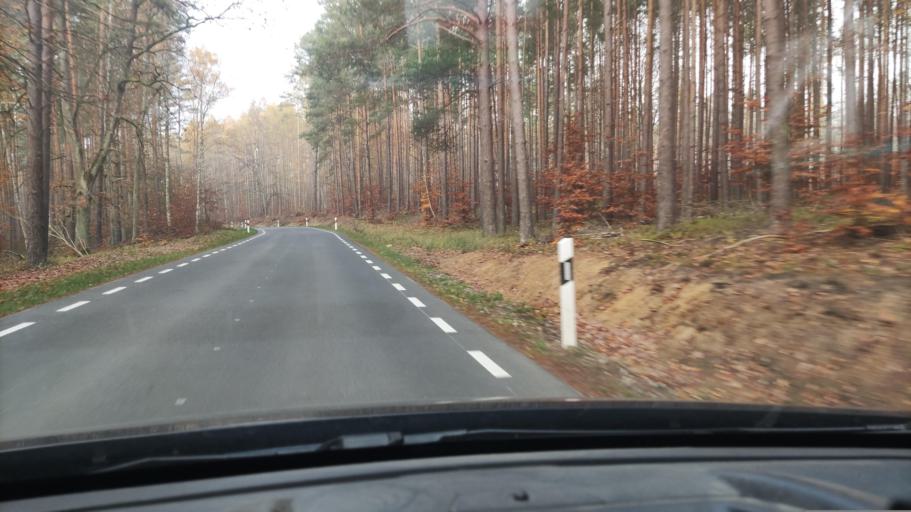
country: DE
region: Brandenburg
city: Furstenberg
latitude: 53.2471
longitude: 13.0987
